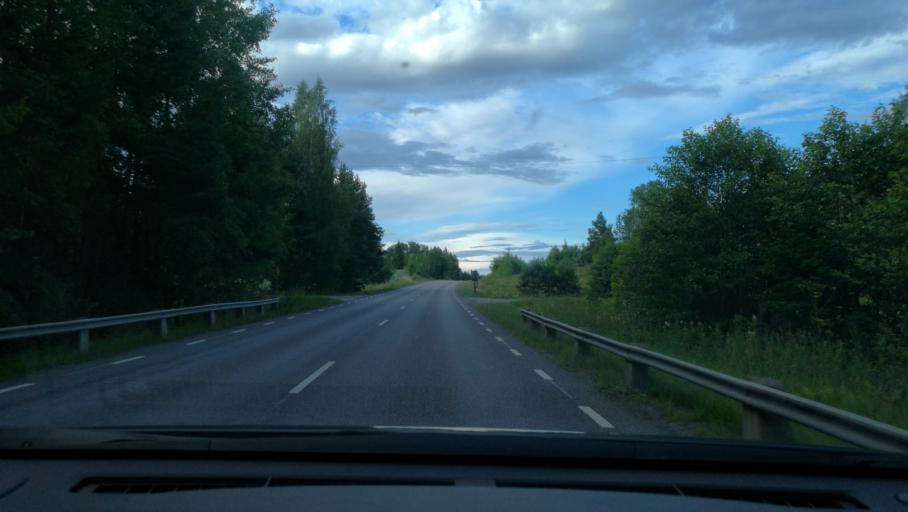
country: SE
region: OEstergoetland
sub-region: Norrkopings Kommun
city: Svartinge
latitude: 58.7085
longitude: 15.9313
